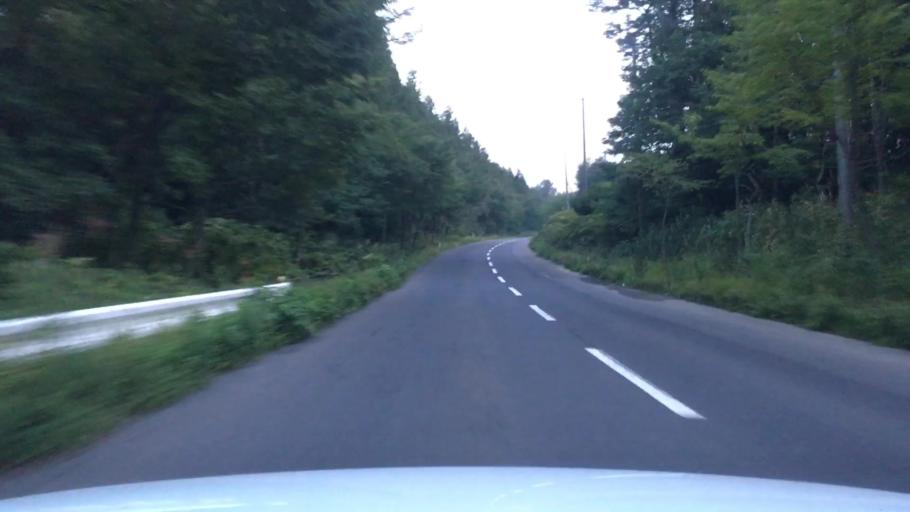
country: JP
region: Aomori
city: Shimokizukuri
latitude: 40.6911
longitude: 140.3616
